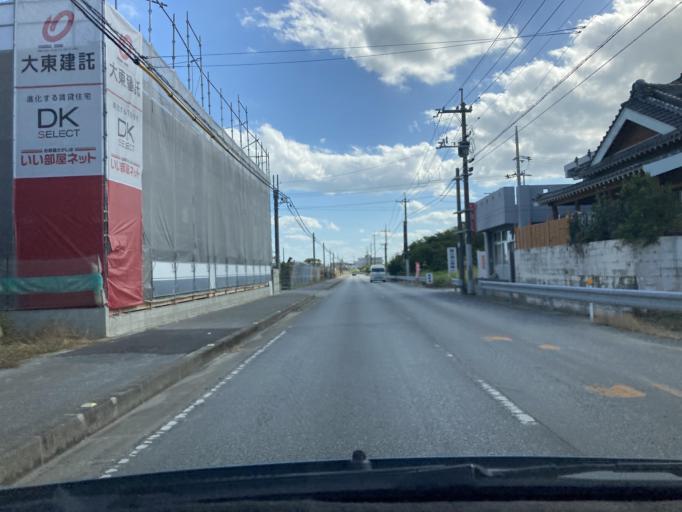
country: JP
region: Okinawa
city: Gushikawa
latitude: 26.3471
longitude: 127.8469
